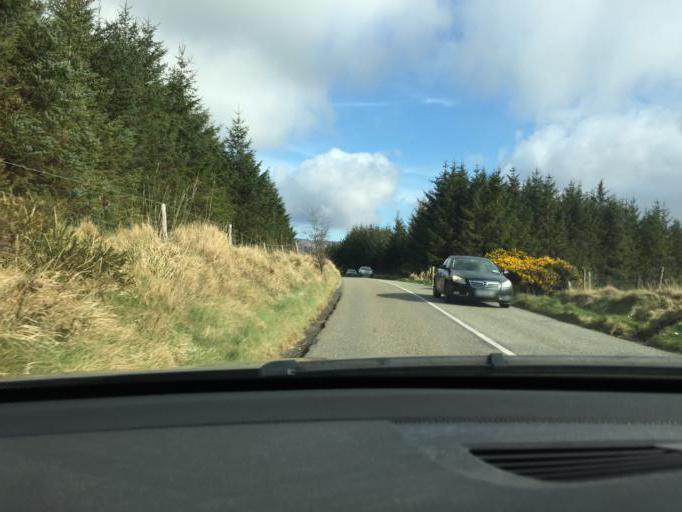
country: IE
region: Leinster
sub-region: Wicklow
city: Valleymount
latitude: 53.0655
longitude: -6.5245
